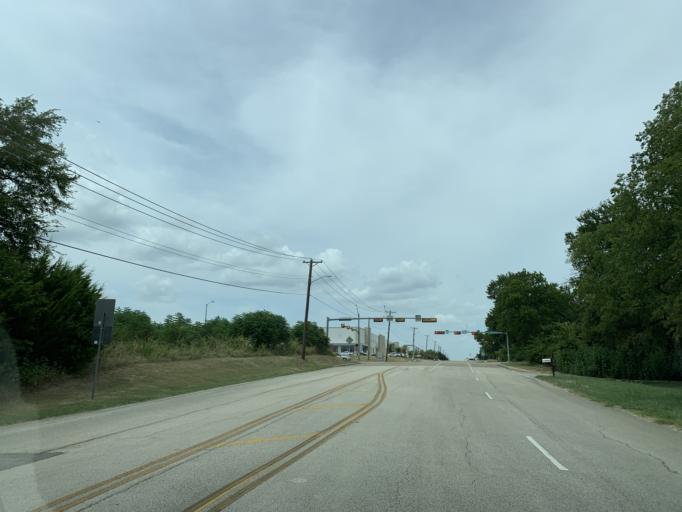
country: US
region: Texas
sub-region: Dallas County
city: Grand Prairie
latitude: 32.6684
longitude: -97.0310
